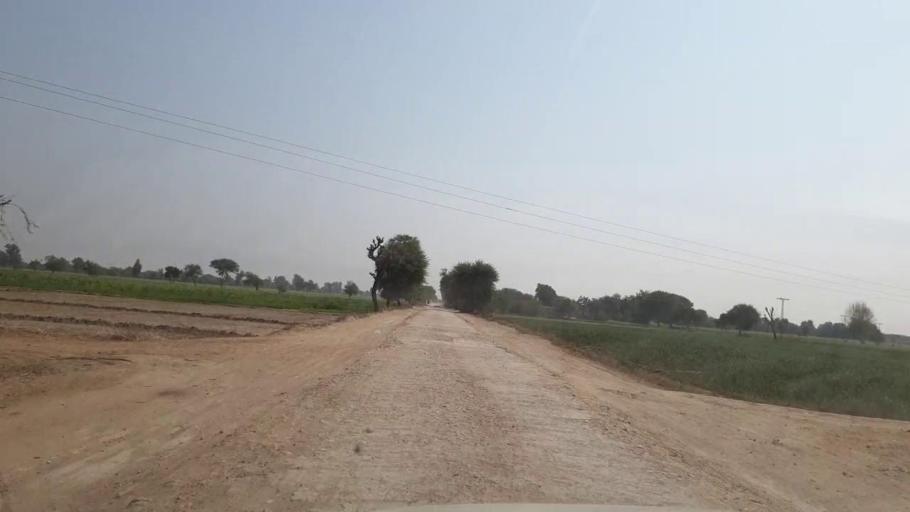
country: PK
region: Sindh
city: Mirpur Khas
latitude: 25.6525
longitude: 69.1459
